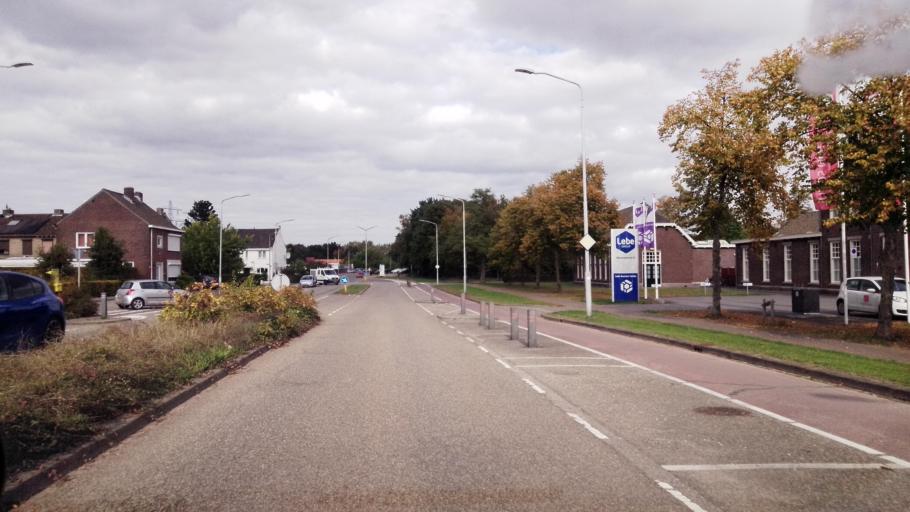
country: NL
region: Limburg
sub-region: Gemeente Venlo
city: Venlo
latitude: 51.3741
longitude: 6.1561
